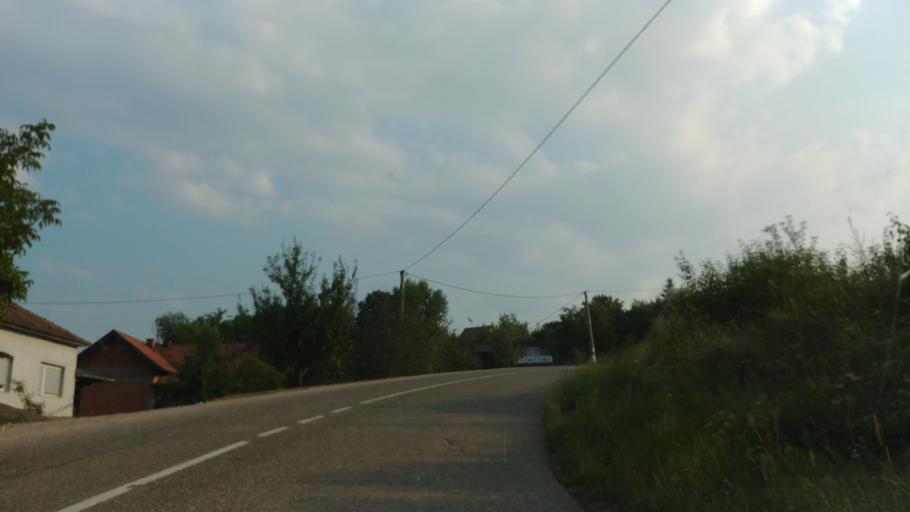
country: BA
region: Republika Srpska
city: Lopare
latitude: 44.7127
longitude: 18.8861
